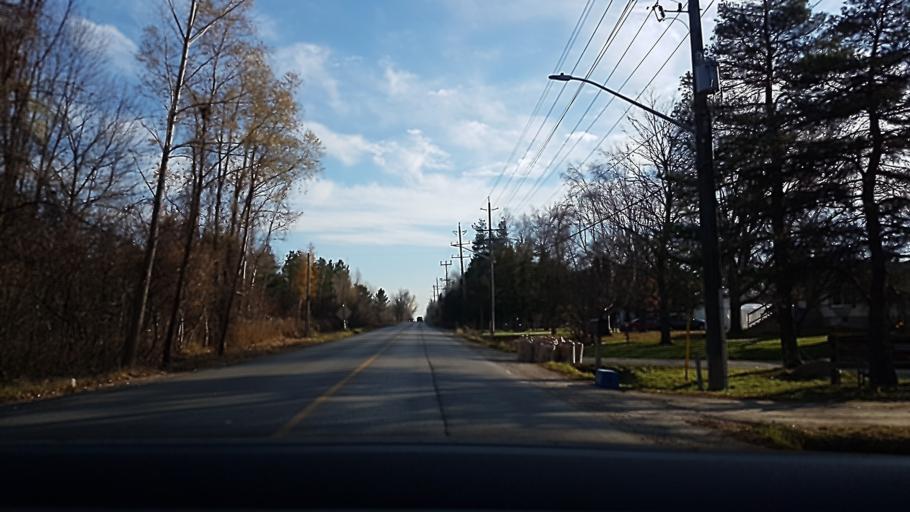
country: CA
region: Ontario
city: Innisfil
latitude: 44.3527
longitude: -79.5490
